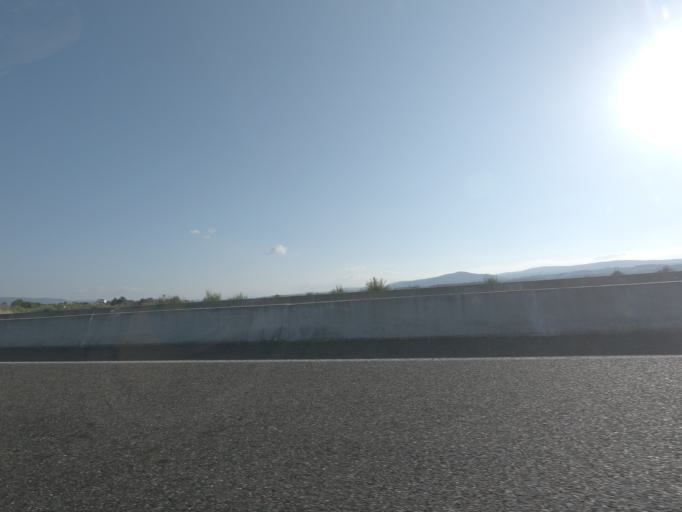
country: ES
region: Galicia
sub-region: Provincia de Ourense
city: Oimbra
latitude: 41.8199
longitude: -7.4179
